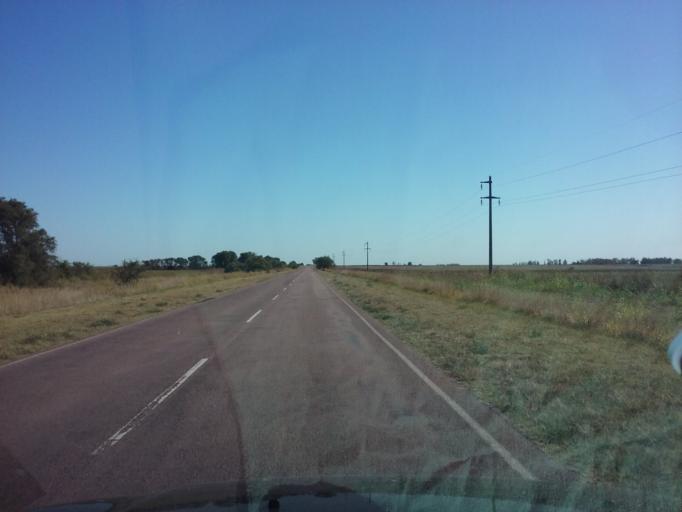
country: AR
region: La Pampa
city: Colonia Baron
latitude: -36.2434
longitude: -63.9426
